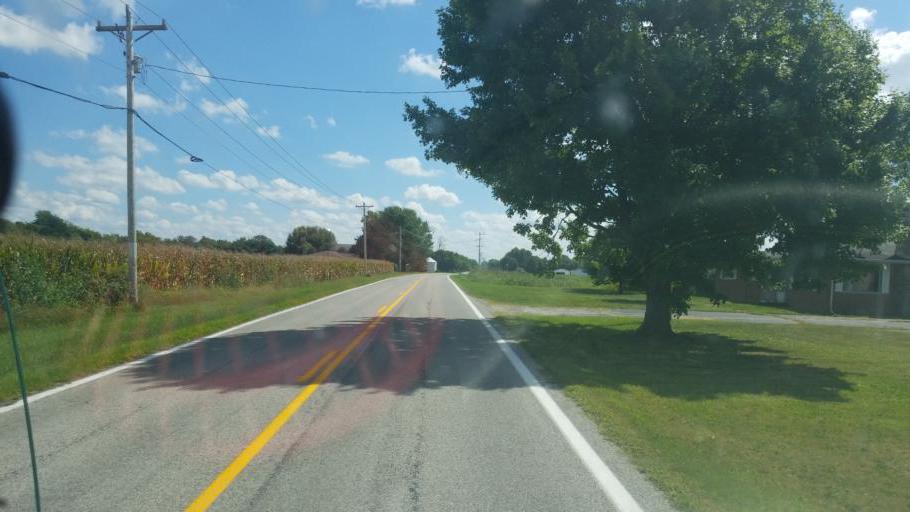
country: US
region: Ohio
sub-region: Marion County
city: Prospect
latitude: 40.3818
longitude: -83.1912
